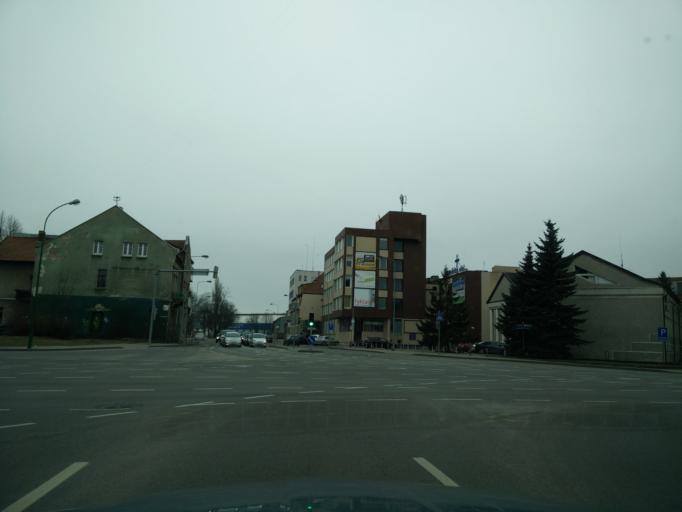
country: LT
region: Klaipedos apskritis
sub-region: Klaipeda
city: Klaipeda
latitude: 55.7027
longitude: 21.1371
